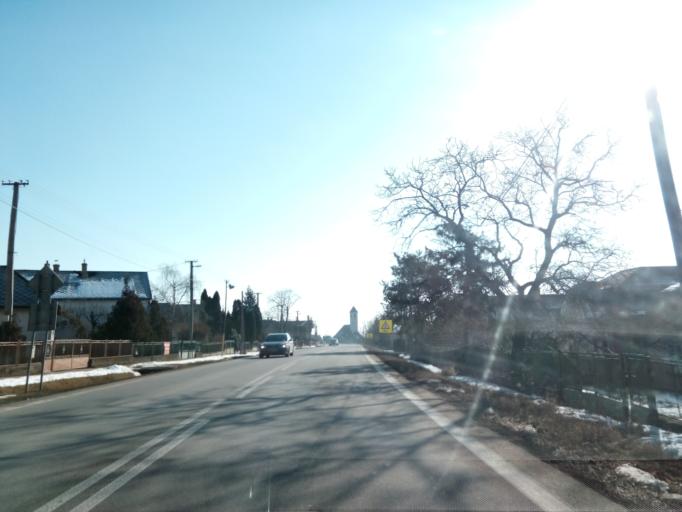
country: SK
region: Kosicky
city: Secovce
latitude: 48.7328
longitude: 21.5821
